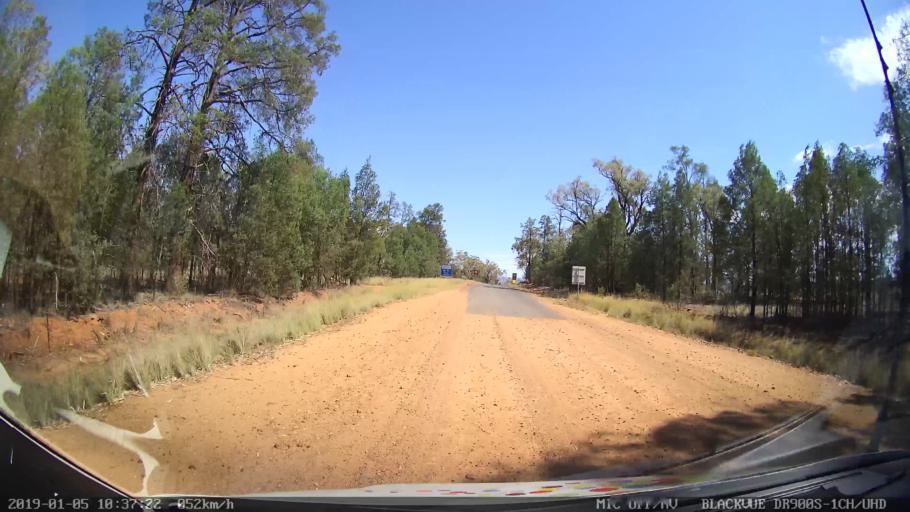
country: AU
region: New South Wales
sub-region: Gilgandra
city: Gilgandra
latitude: -31.4751
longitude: 148.9217
